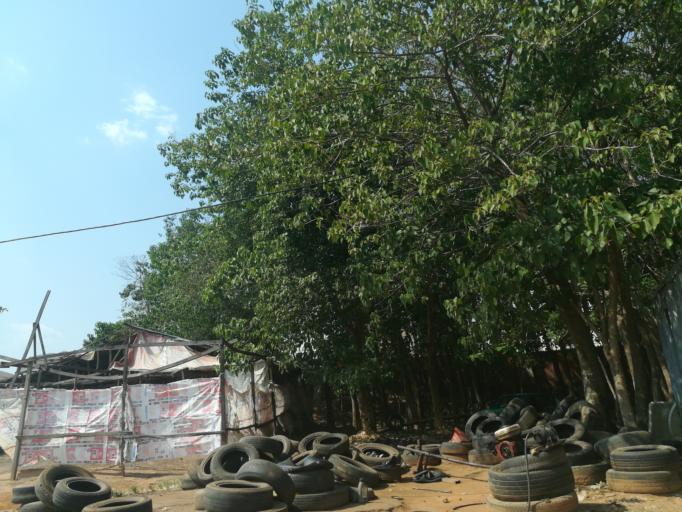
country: NG
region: Abuja Federal Capital Territory
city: Abuja
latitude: 9.0603
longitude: 7.4272
